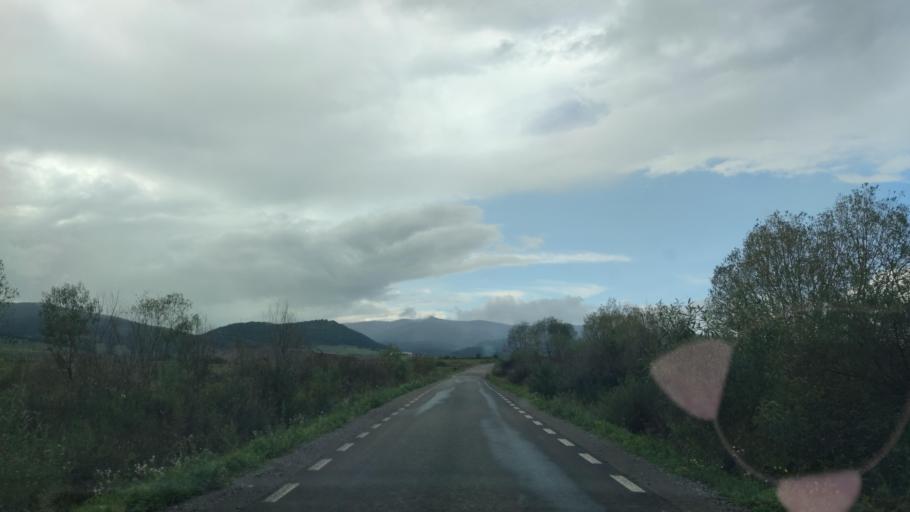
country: RO
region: Harghita
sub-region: Comuna Remetea
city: Remetea
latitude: 46.8079
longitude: 25.4090
